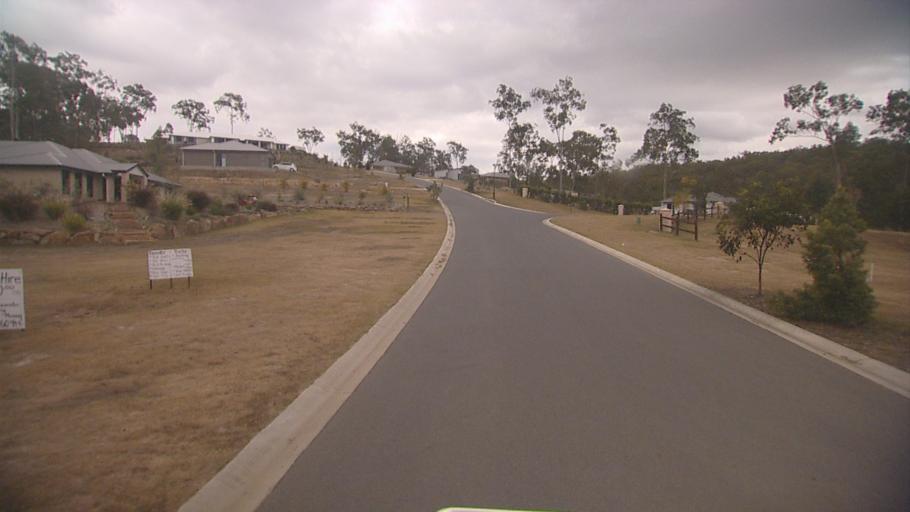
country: AU
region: Queensland
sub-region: Logan
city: Cedar Vale
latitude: -27.8610
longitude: 153.0782
